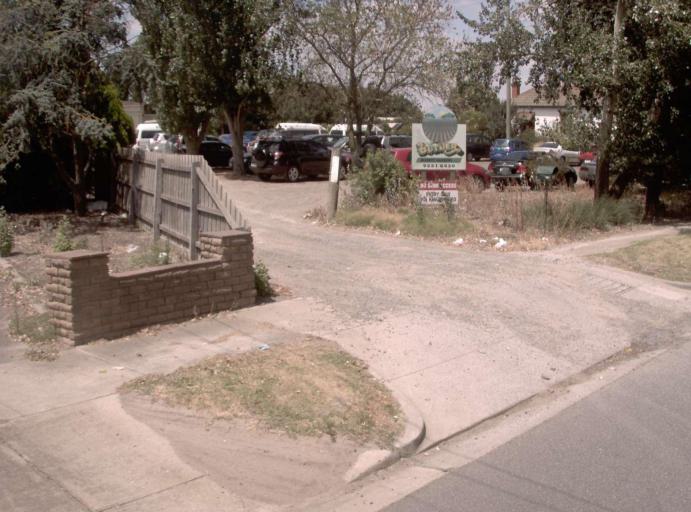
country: AU
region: Victoria
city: Heatherton
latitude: -37.9581
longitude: 145.1010
